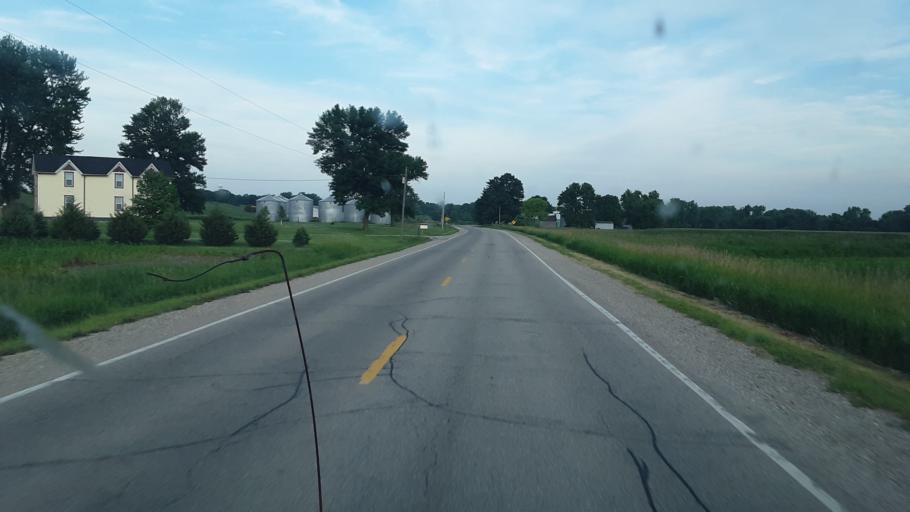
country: US
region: Iowa
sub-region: Benton County
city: Belle Plaine
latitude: 41.9369
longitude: -92.4062
